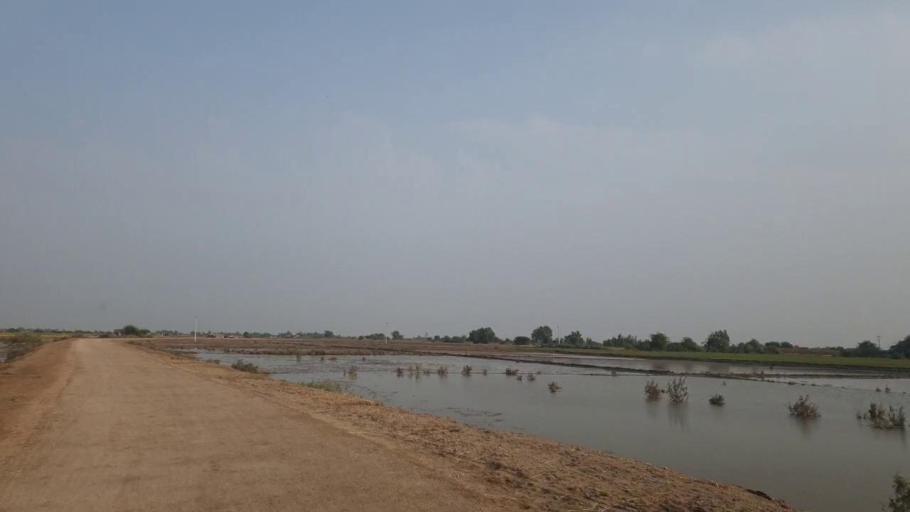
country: PK
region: Sindh
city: Badin
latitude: 24.6002
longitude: 68.6979
